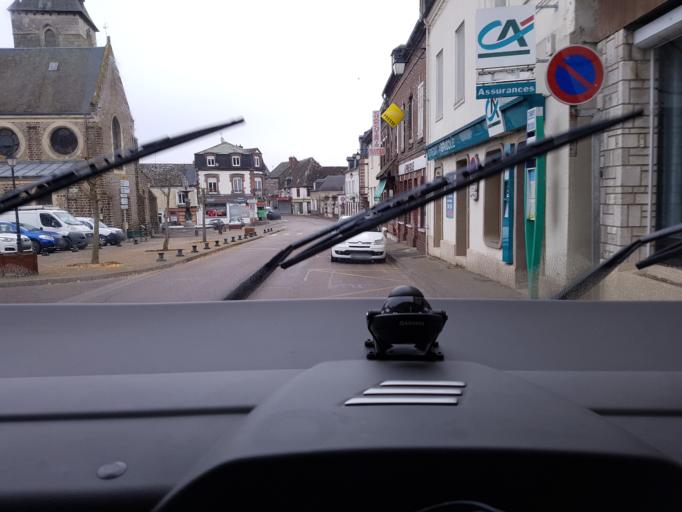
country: FR
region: Haute-Normandie
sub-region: Departement de l'Eure
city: Rugles
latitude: 48.9075
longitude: 0.7489
